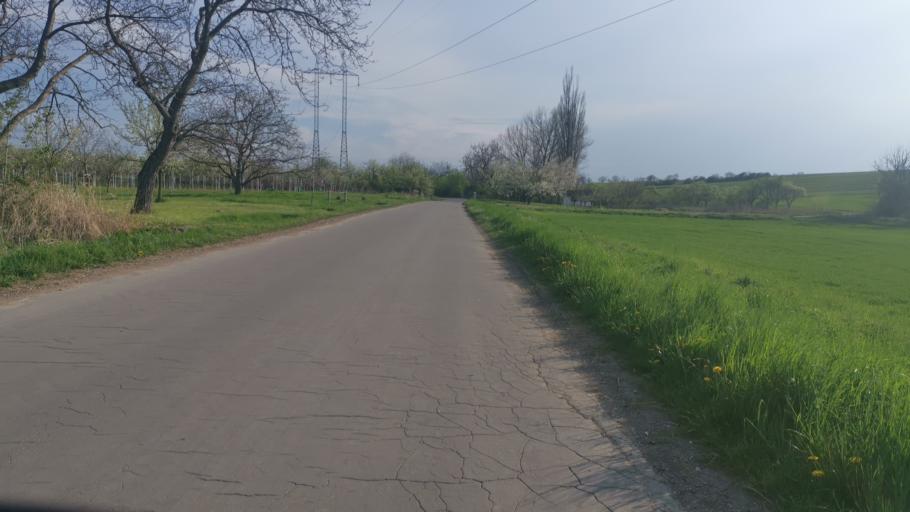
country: CZ
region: South Moravian
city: Petrov
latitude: 48.8575
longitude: 17.3077
